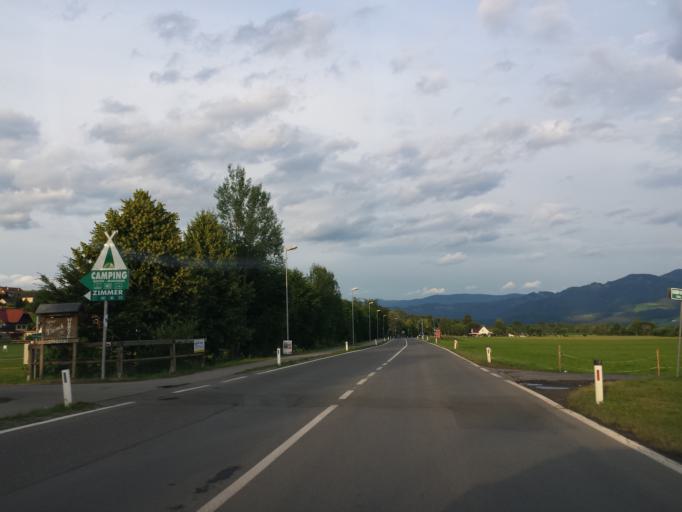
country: AT
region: Styria
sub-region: Politischer Bezirk Murtal
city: Spielberg bei Knittelfeld
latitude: 47.2155
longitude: 14.7680
